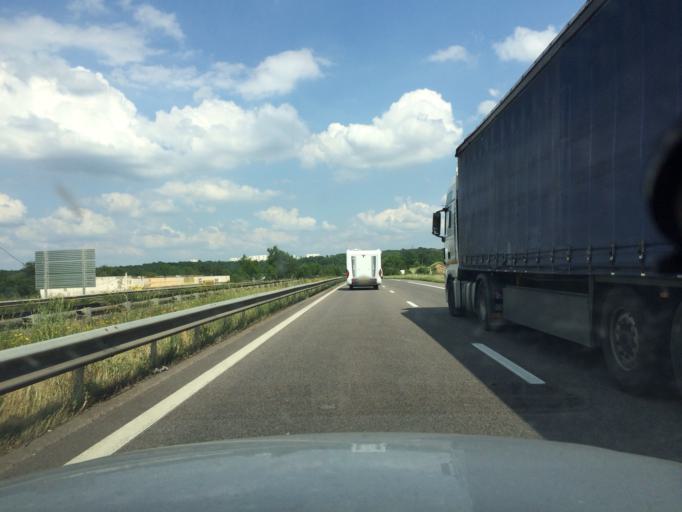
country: FR
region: Lorraine
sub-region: Departement de Meurthe-et-Moselle
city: Laxou
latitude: 48.6941
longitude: 6.0968
